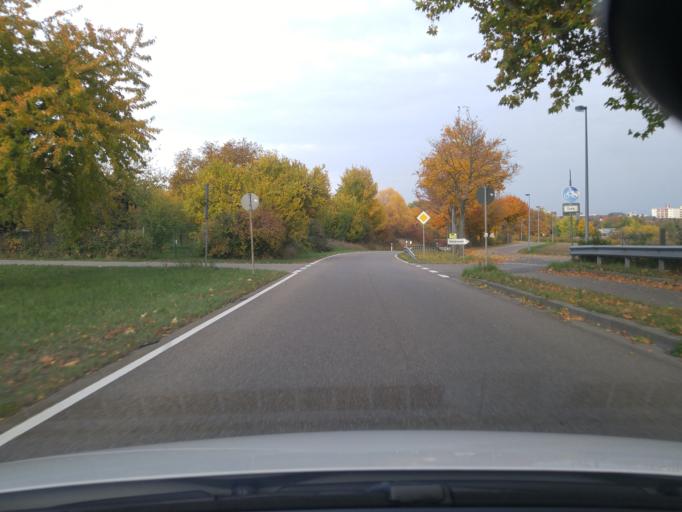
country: DE
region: Rheinland-Pfalz
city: Speyer
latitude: 49.3042
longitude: 8.4154
